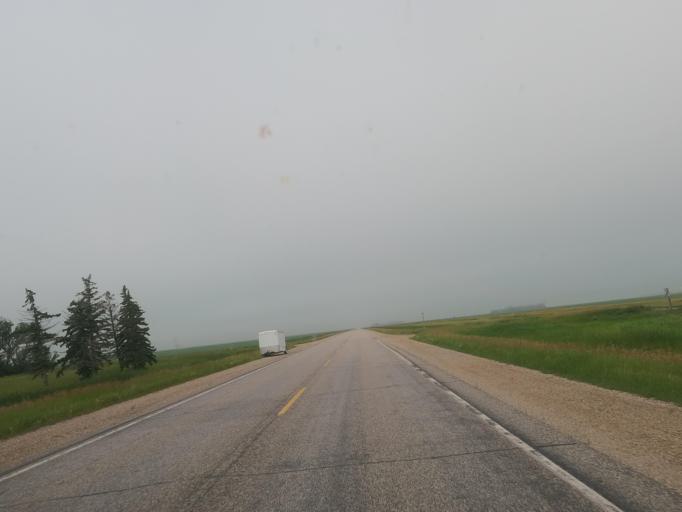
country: CA
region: Manitoba
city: Carman
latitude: 49.7351
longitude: -97.8456
